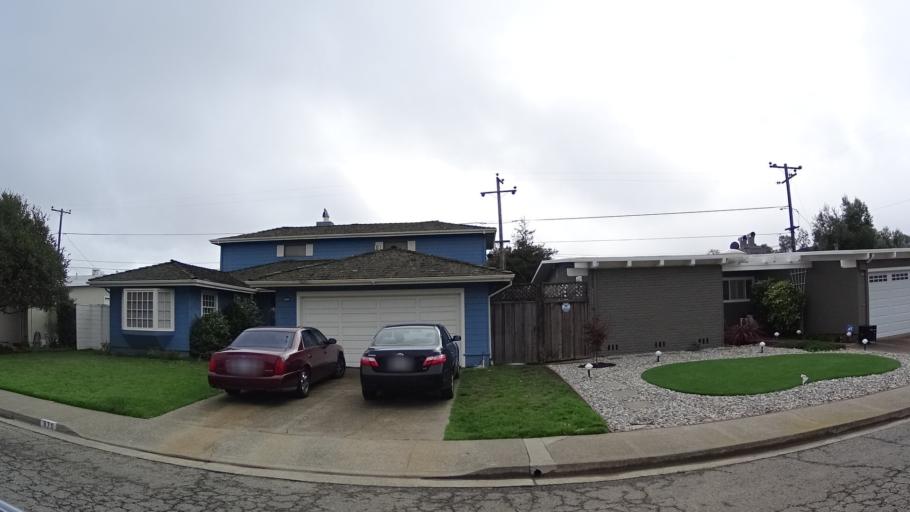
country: US
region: California
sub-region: San Mateo County
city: San Bruno
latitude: 37.6057
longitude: -122.4215
